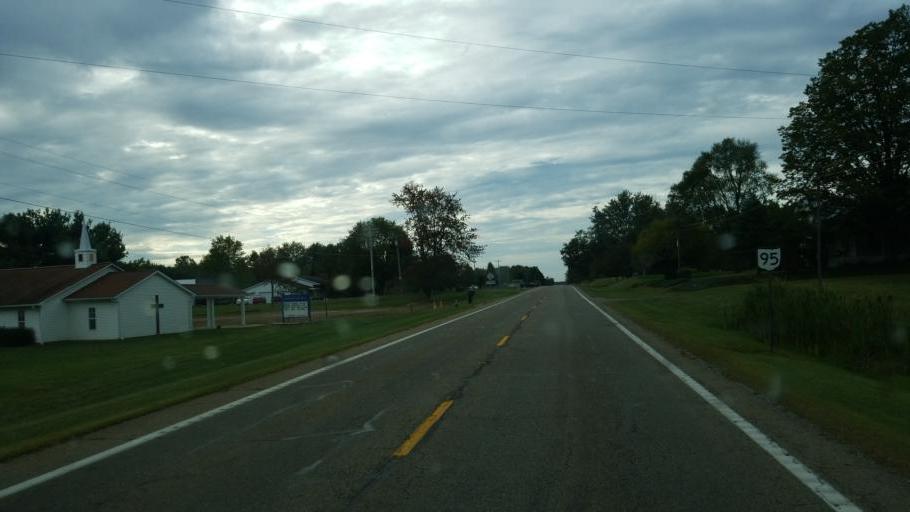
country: US
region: Ohio
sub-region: Morrow County
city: Mount Gilead
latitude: 40.5151
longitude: -82.7438
